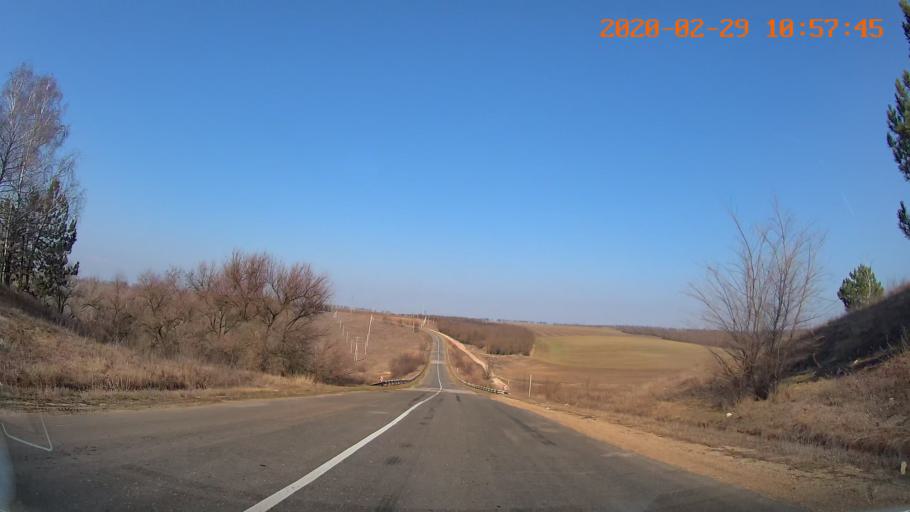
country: MD
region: Telenesti
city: Grigoriopol
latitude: 47.1630
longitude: 29.3208
